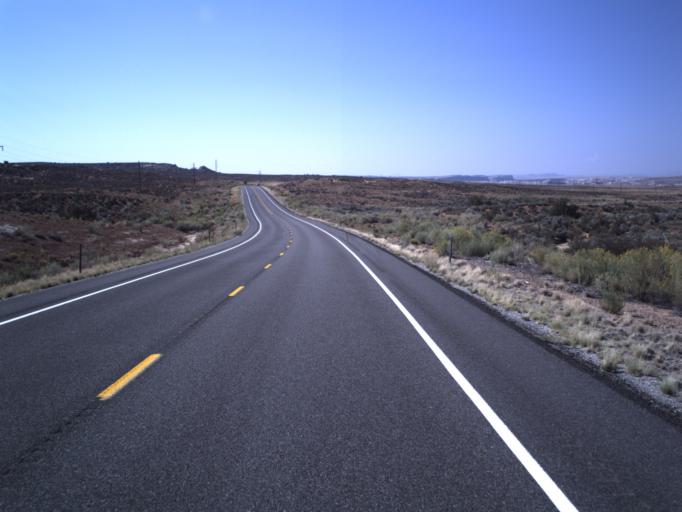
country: US
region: Utah
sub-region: San Juan County
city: Blanding
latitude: 37.3745
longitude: -109.5053
